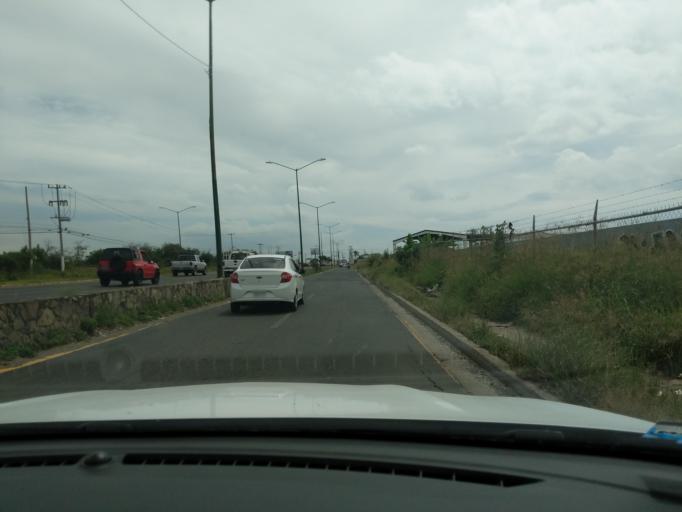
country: MX
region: Jalisco
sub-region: Zapopan
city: Puerta del Llano
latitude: 20.7839
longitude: -103.4663
